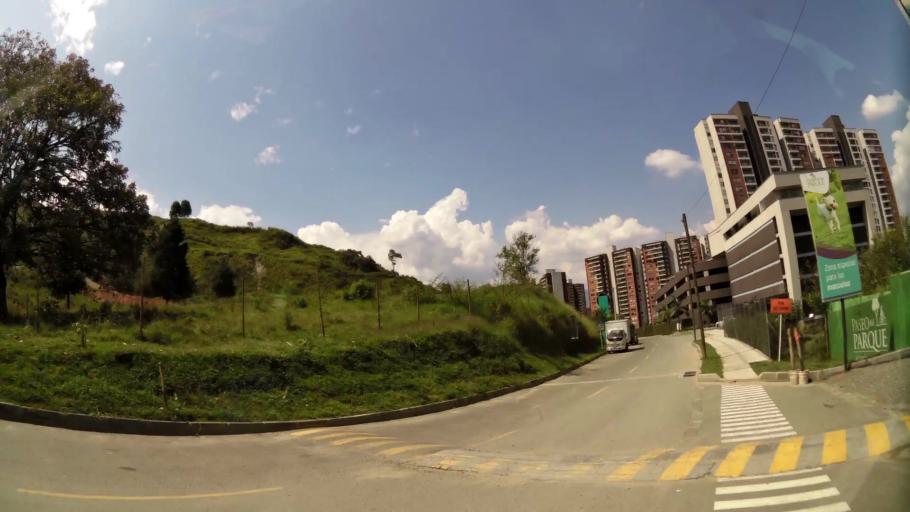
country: CO
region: Antioquia
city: Itagui
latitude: 6.2126
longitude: -75.6076
